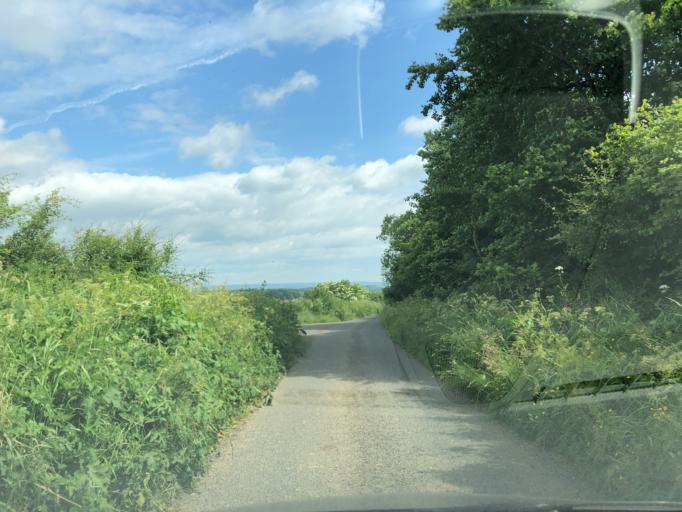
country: GB
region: England
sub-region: North Yorkshire
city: Helmsley
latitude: 54.1500
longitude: -1.0117
